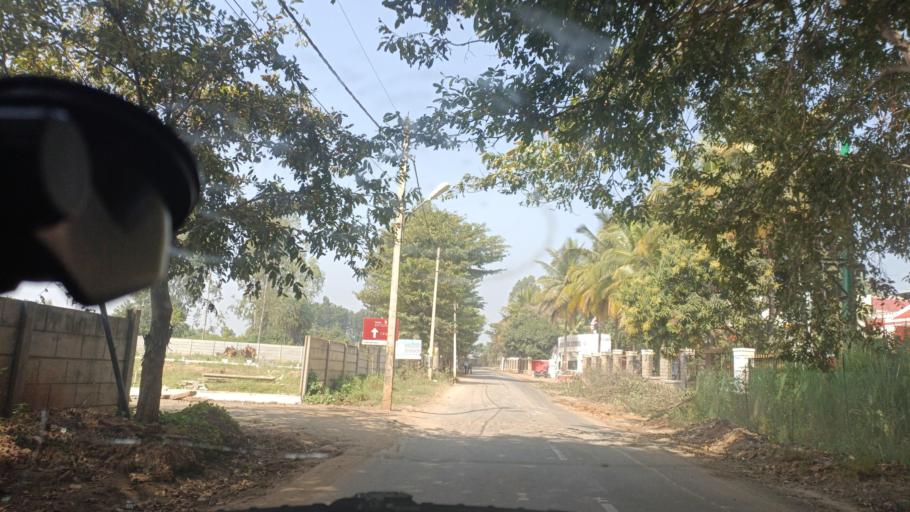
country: IN
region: Karnataka
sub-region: Bangalore Urban
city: Yelahanka
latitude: 13.1228
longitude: 77.6018
